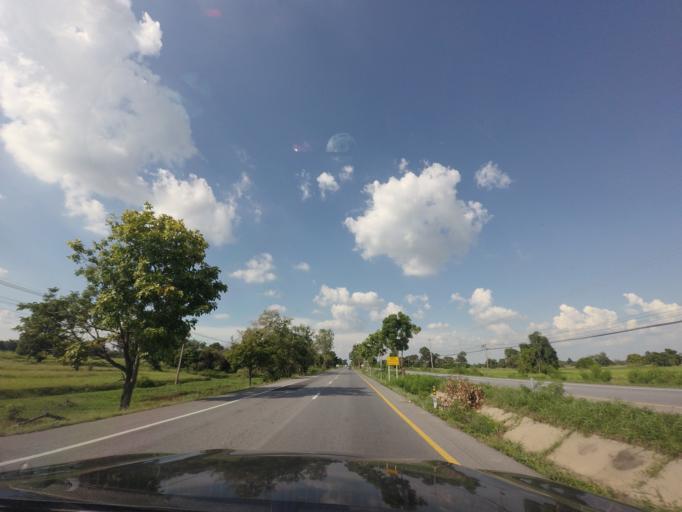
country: TH
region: Khon Kaen
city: Phon
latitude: 15.7171
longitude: 102.5902
